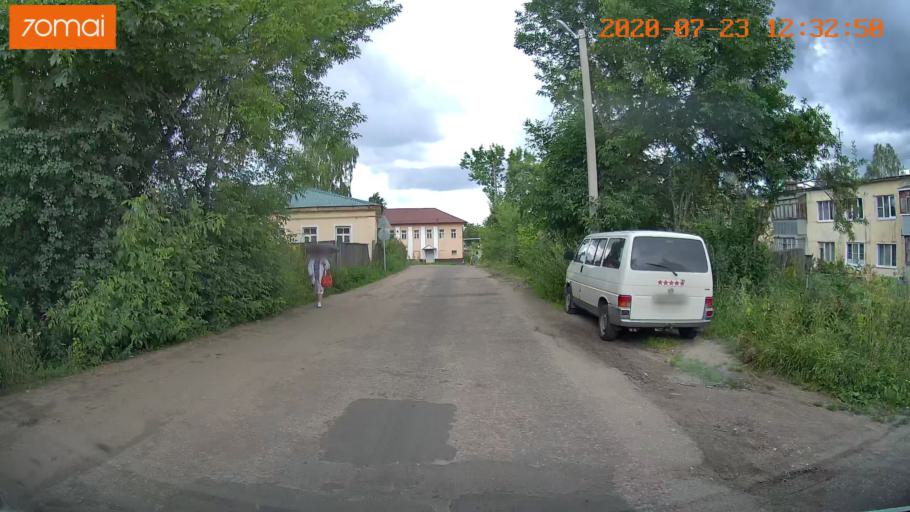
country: RU
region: Ivanovo
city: Bogorodskoye
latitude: 57.0472
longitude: 41.0062
